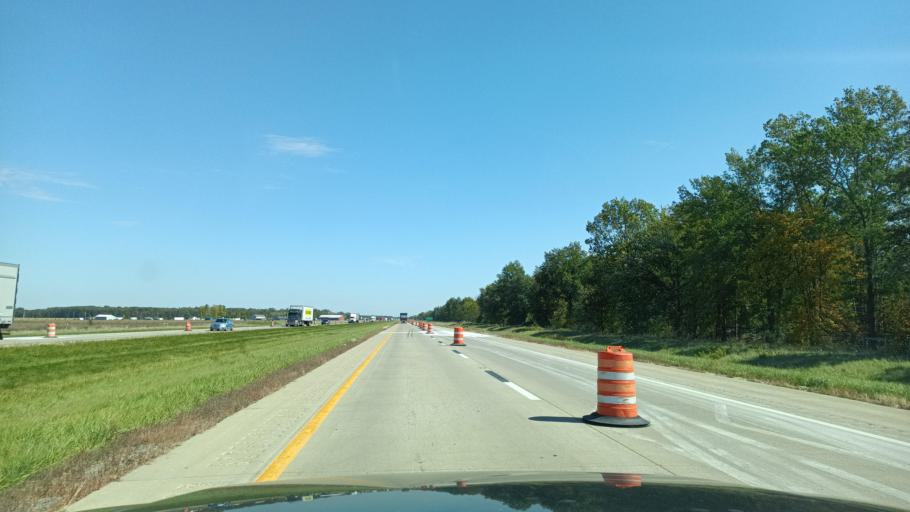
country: US
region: Ohio
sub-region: Defiance County
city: Defiance
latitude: 41.2477
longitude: -84.4903
